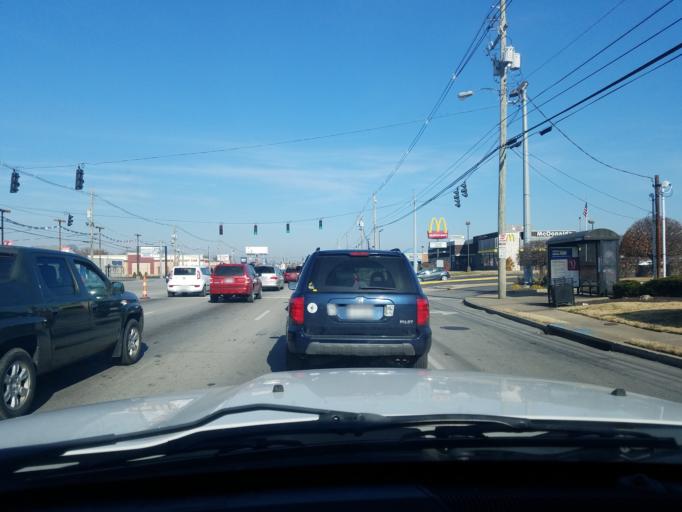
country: US
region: Kentucky
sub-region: Jefferson County
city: Pleasure Ridge Park
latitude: 38.1517
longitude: -85.8363
